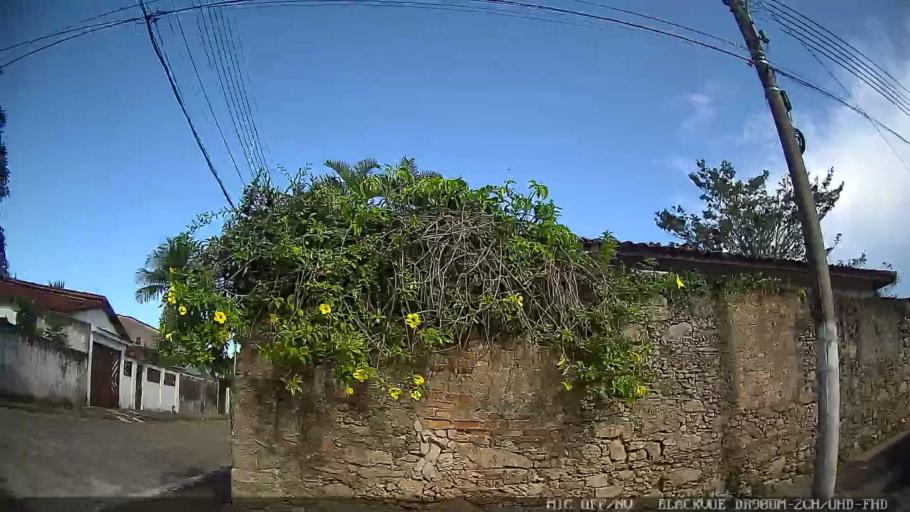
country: BR
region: Sao Paulo
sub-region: Iguape
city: Iguape
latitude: -24.7092
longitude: -47.5583
